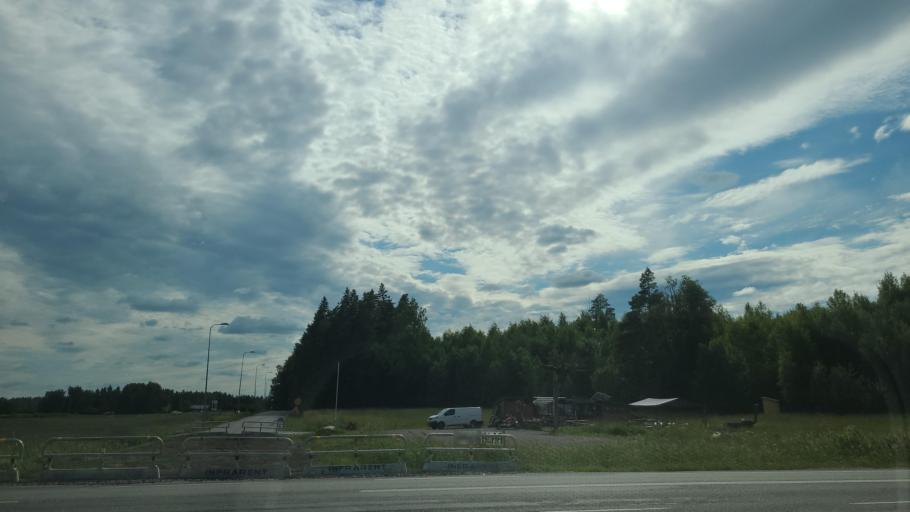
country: FI
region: Varsinais-Suomi
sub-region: Turku
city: Naantali
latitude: 60.4595
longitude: 21.9829
